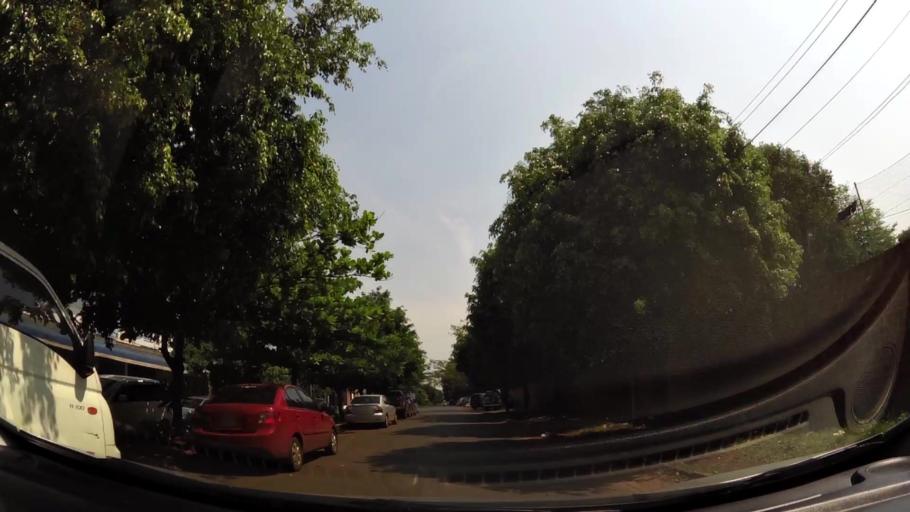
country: PY
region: Alto Parana
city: Presidente Franco
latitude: -25.5248
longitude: -54.6183
